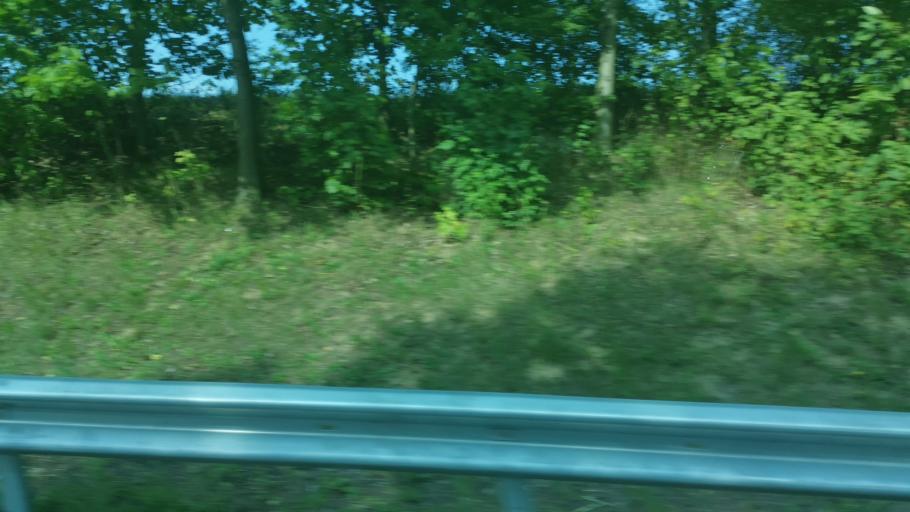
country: DE
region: Bavaria
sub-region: Upper Palatinate
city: Willmering
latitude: 49.2364
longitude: 12.6745
